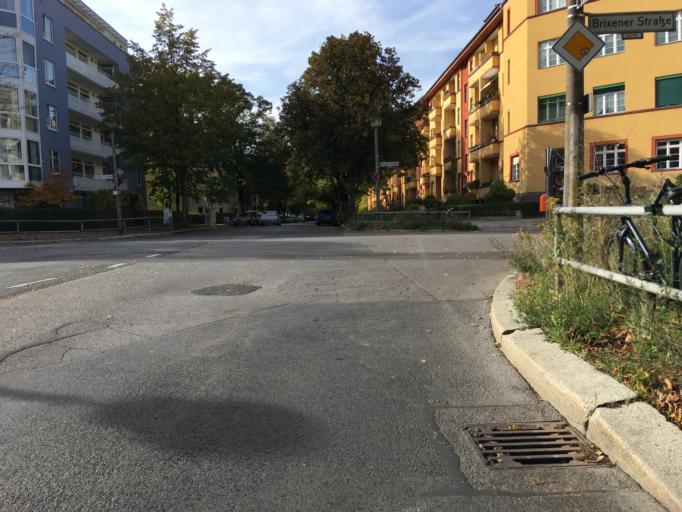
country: DE
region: Berlin
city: Pankow
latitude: 52.5613
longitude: 13.4075
